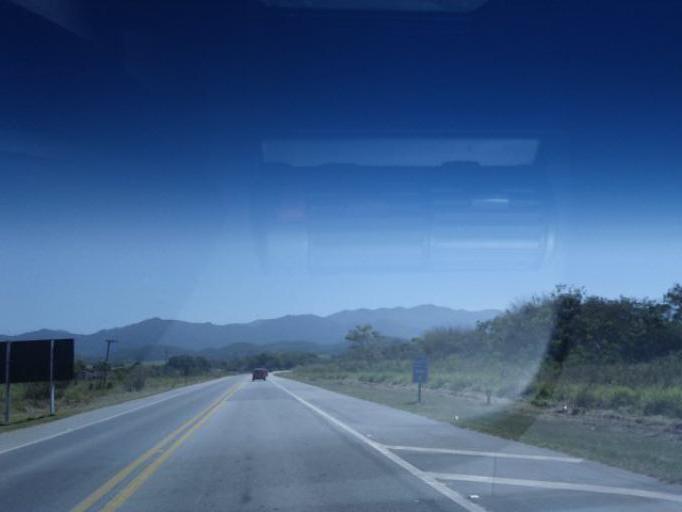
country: BR
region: Sao Paulo
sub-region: Taubate
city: Taubate
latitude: -22.9911
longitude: -45.6460
